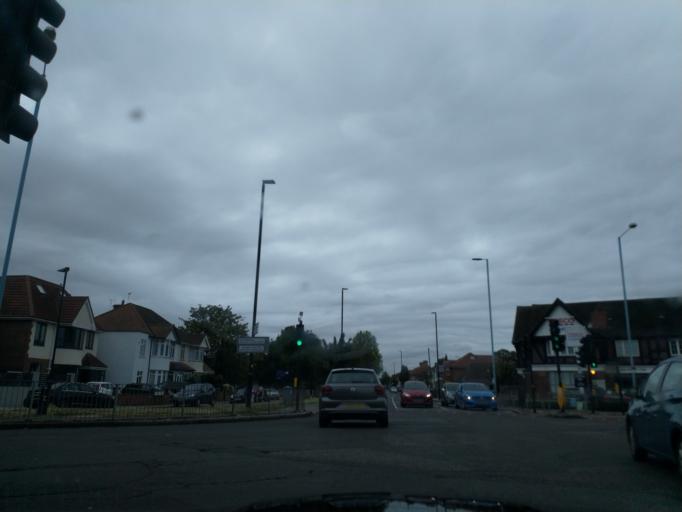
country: GB
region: England
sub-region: Greater London
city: Hounslow
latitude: 51.4569
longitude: -0.3725
